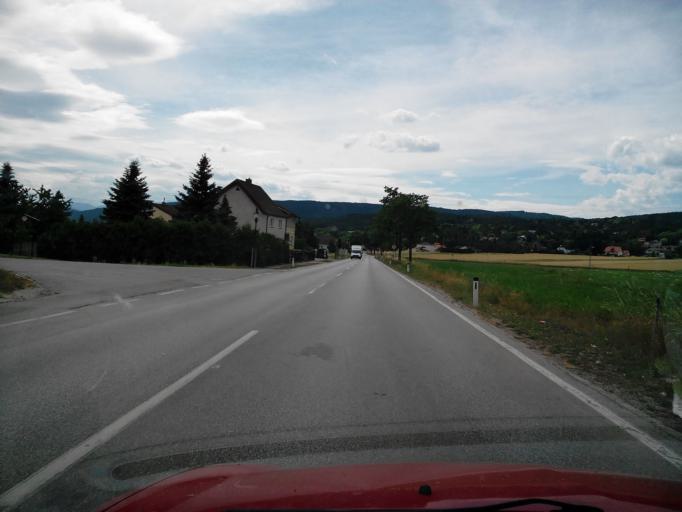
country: AT
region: Lower Austria
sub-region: Politischer Bezirk Wiener Neustadt
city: Weikersdorf am Steinfelde
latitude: 47.8350
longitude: 16.1818
